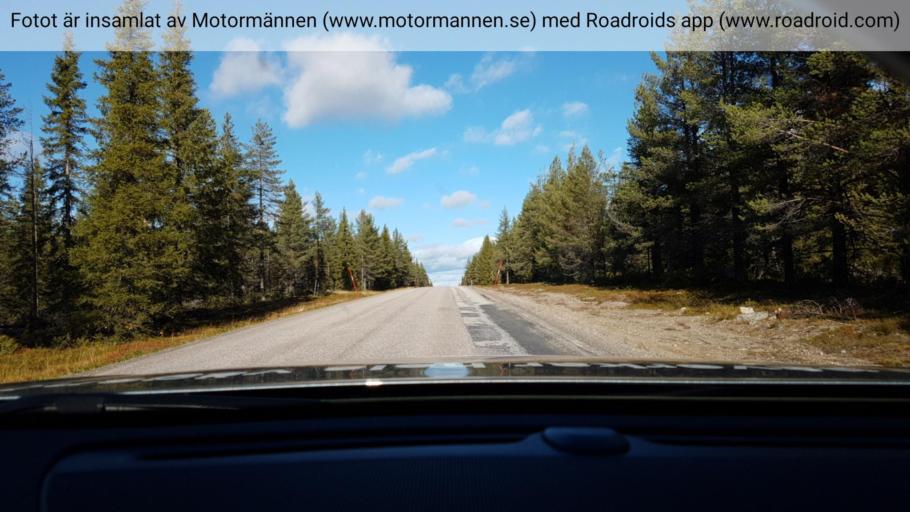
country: SE
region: Norrbotten
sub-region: Arjeplogs Kommun
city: Arjeplog
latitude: 65.8312
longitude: 18.4324
